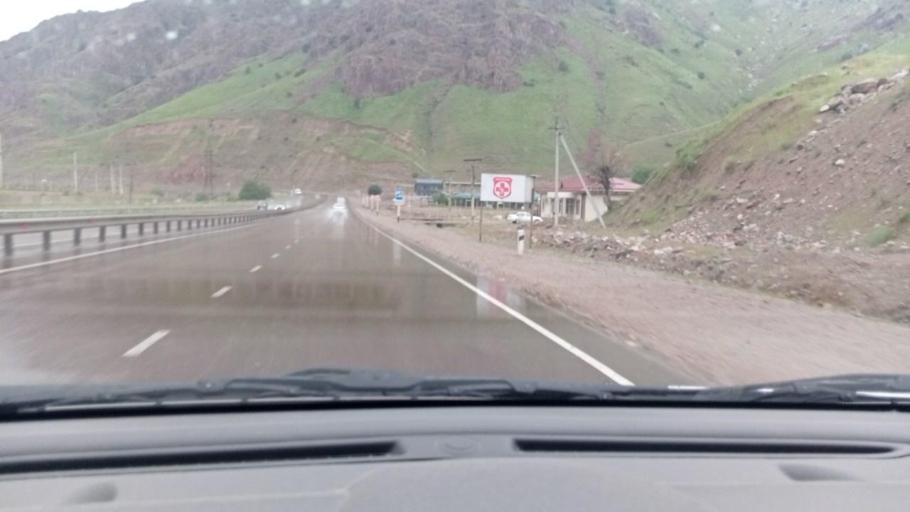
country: UZ
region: Toshkent
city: Angren
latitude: 41.1260
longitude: 70.3629
